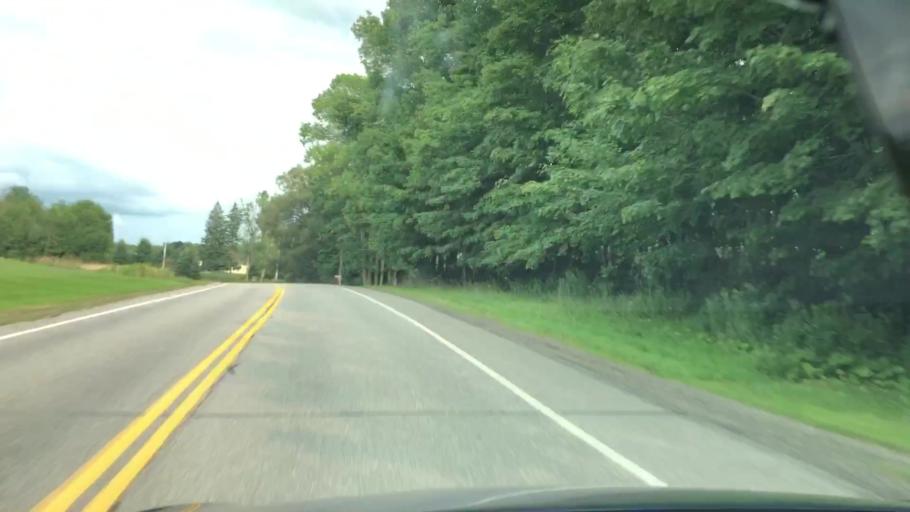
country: US
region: Pennsylvania
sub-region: Erie County
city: Northwest Harborcreek
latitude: 42.0564
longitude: -79.9009
